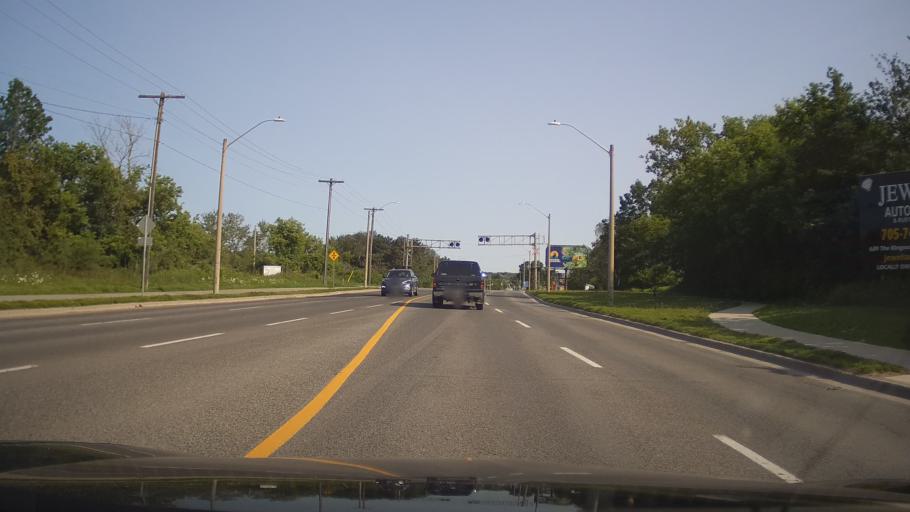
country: CA
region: Ontario
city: Peterborough
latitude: 44.2777
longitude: -78.3417
